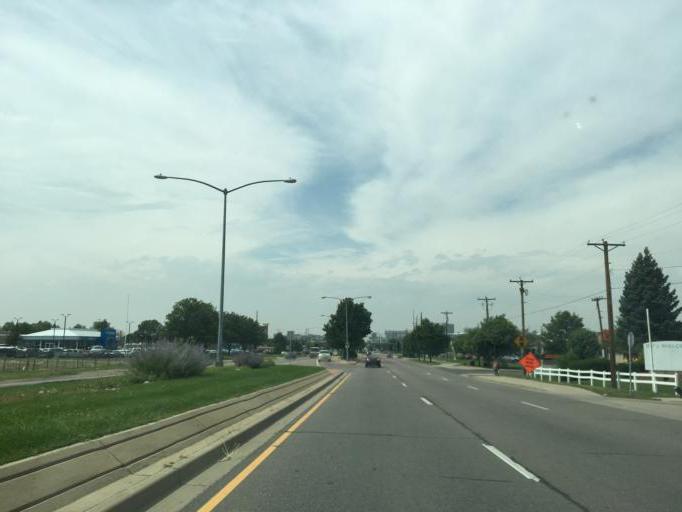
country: US
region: Colorado
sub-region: Adams County
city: Aurora
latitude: 39.7401
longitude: -104.8160
